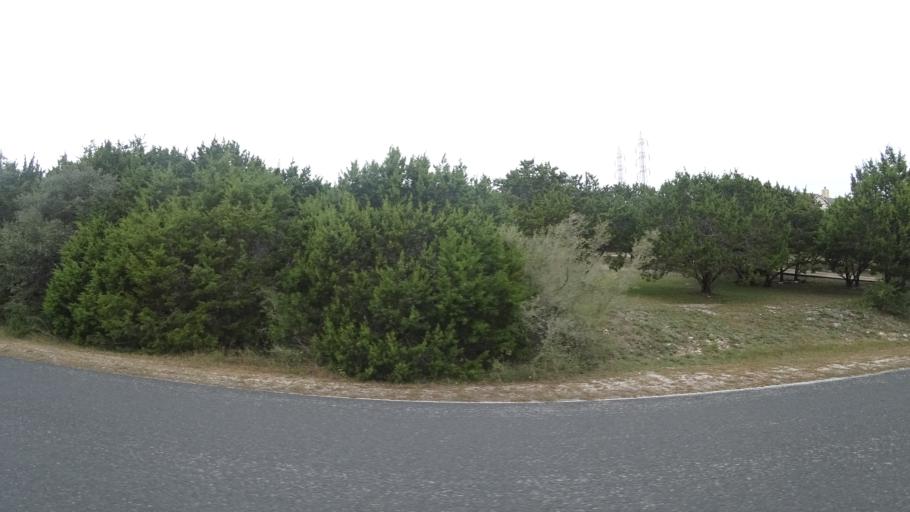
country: US
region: Texas
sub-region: Travis County
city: Hudson Bend
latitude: 30.3897
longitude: -97.9169
